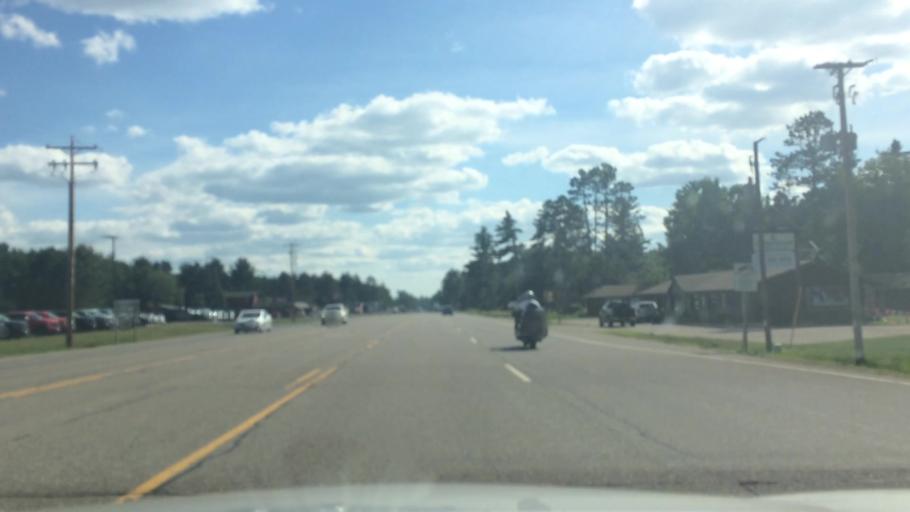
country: US
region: Wisconsin
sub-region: Vilas County
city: Lac du Flambeau
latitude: 45.8320
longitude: -89.7150
